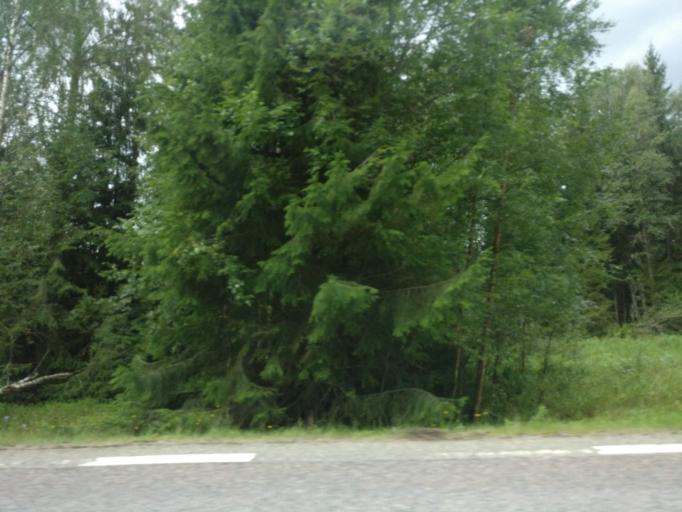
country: SE
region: Vaermland
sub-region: Torsby Kommun
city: Torsby
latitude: 60.7730
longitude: 12.7518
